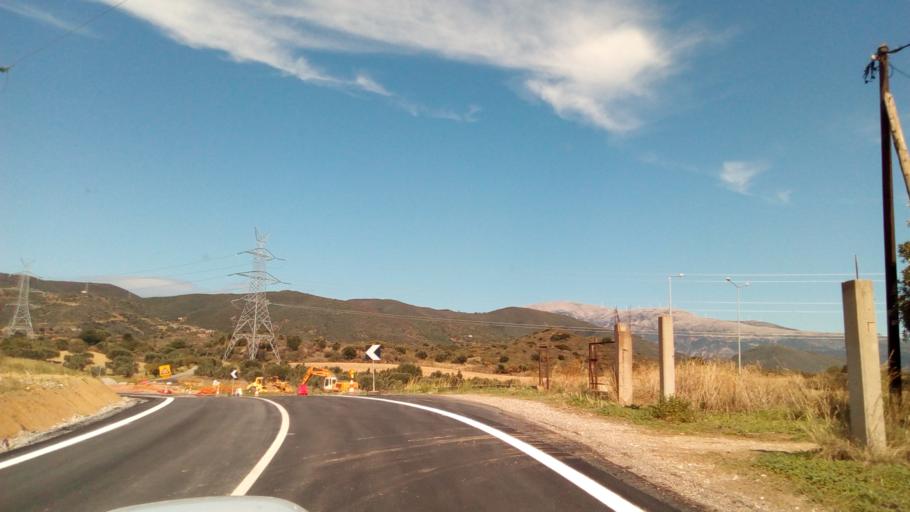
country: GR
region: West Greece
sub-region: Nomos Aitolias kai Akarnanias
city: Antirrio
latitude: 38.3444
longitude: 21.7554
